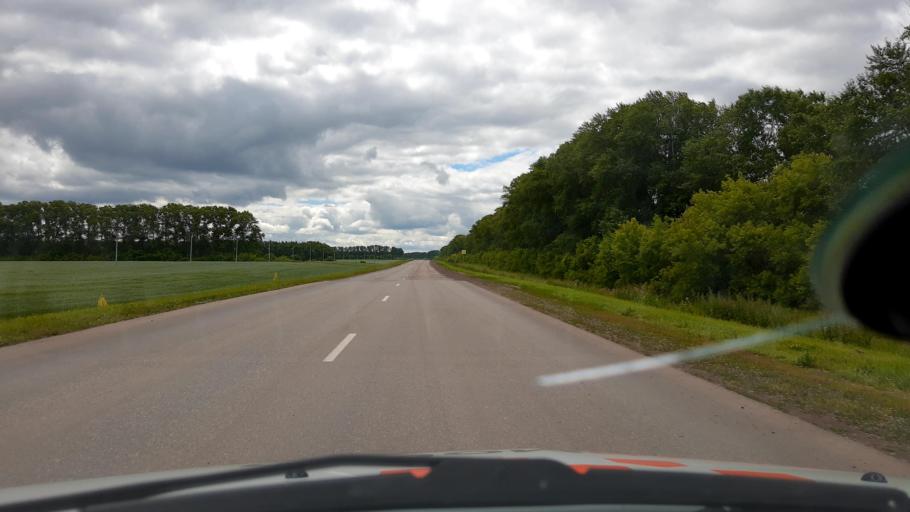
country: RU
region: Bashkortostan
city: Buzdyak
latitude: 54.6804
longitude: 54.5515
